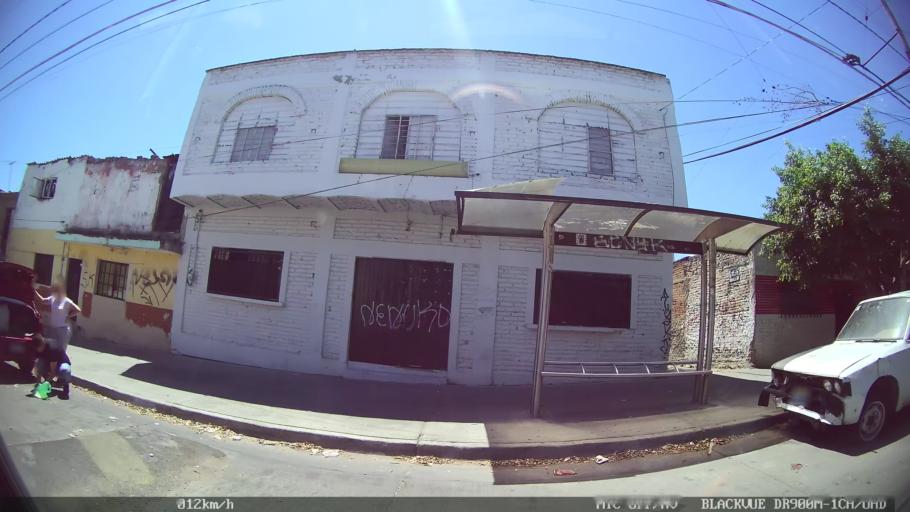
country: MX
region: Jalisco
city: Tlaquepaque
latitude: 20.6830
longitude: -103.2918
